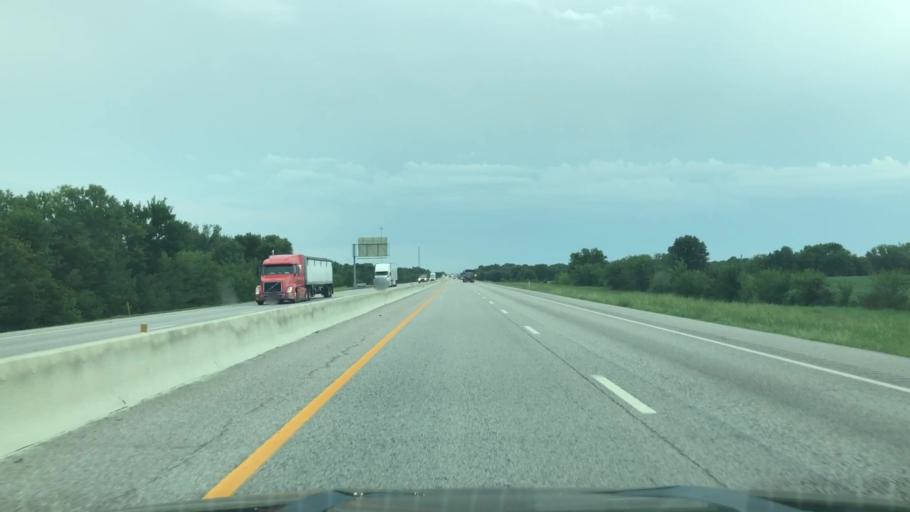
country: US
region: Oklahoma
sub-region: Craig County
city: Vinita
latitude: 36.5922
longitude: -95.1965
